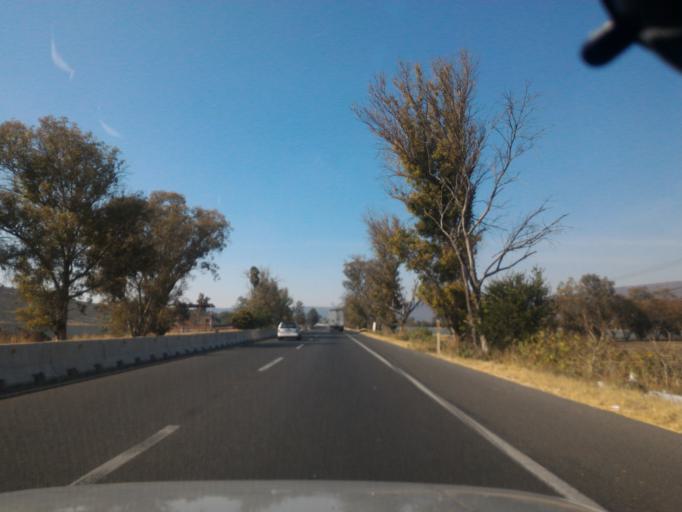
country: MX
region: Jalisco
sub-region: Poncitlan
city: Cuitzeo (La Estancia)
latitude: 20.3584
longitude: -102.8014
